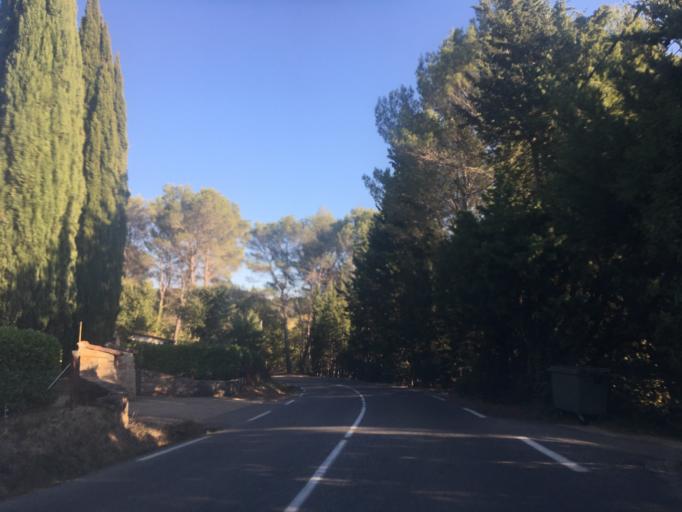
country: FR
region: Provence-Alpes-Cote d'Azur
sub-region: Departement du Var
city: Villecroze
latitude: 43.5691
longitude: 6.2859
